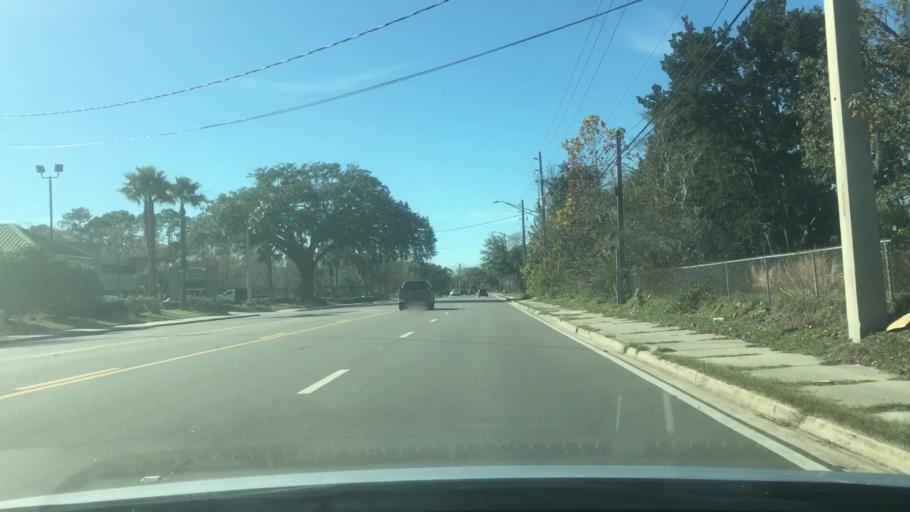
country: US
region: Florida
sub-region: Duval County
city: Jacksonville
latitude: 30.4672
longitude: -81.6228
